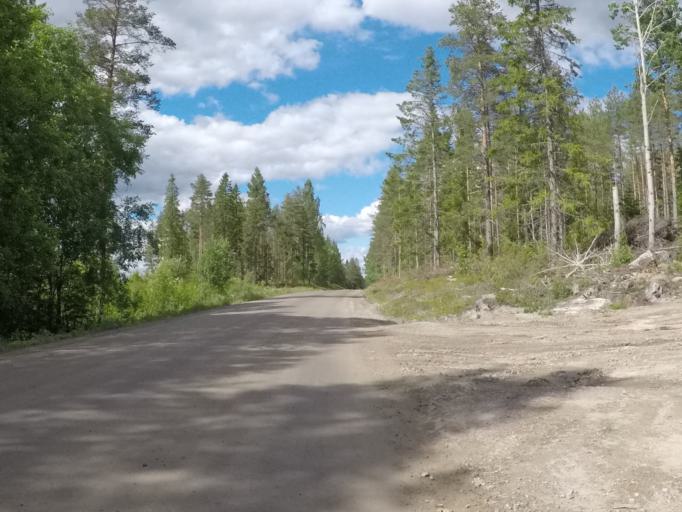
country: SE
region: Vaesterbotten
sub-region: Robertsfors Kommun
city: Robertsfors
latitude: 64.1354
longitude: 20.9028
